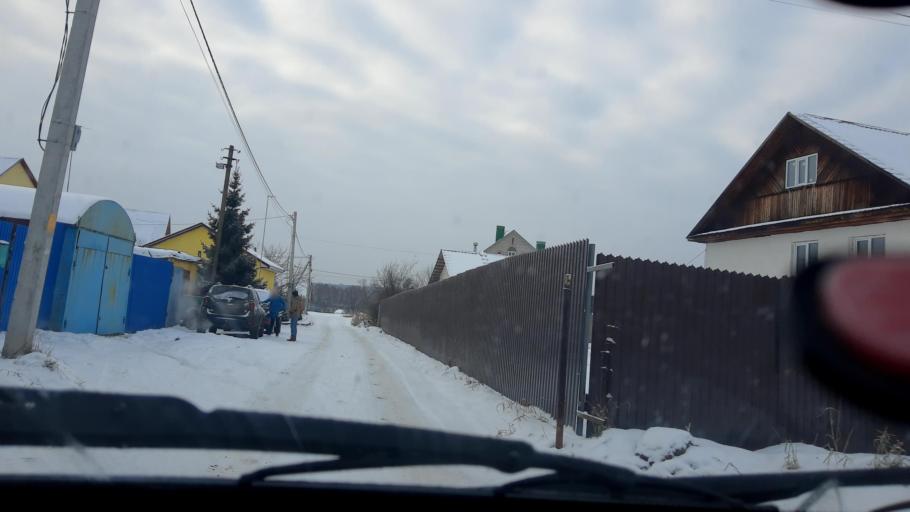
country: RU
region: Bashkortostan
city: Iglino
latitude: 54.7434
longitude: 56.2812
